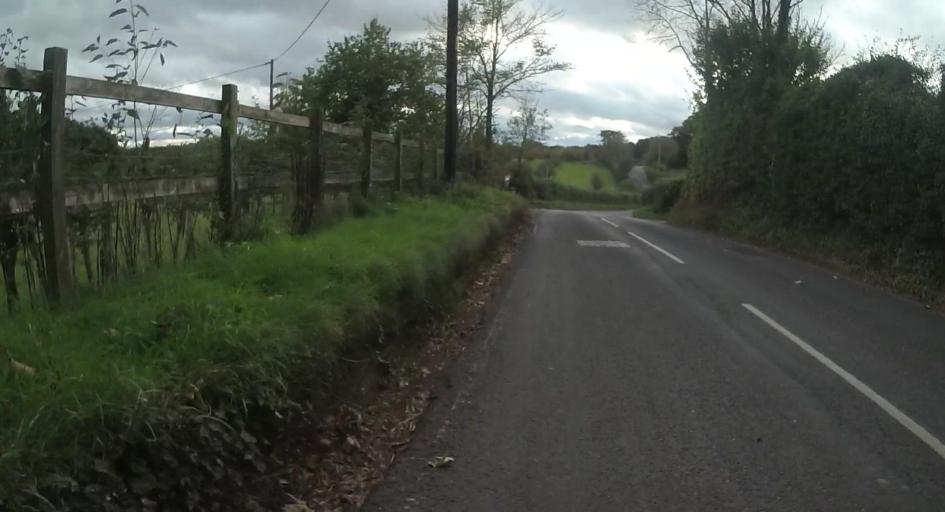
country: GB
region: England
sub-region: Hampshire
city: Andover
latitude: 51.1896
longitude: -1.4034
